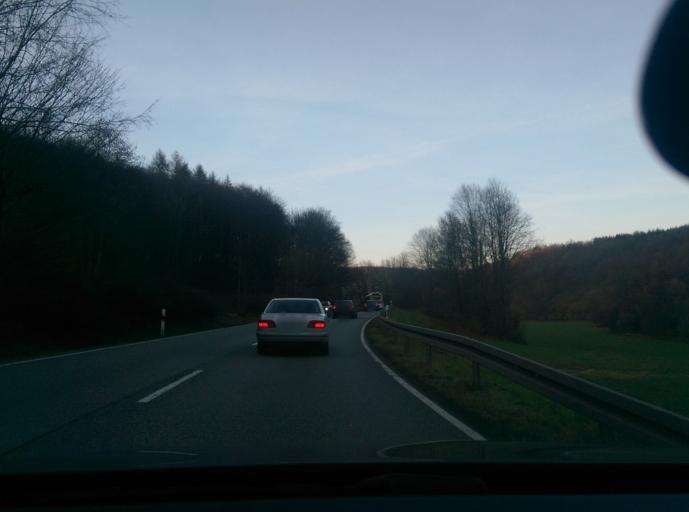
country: DE
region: Hesse
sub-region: Regierungsbezirk Kassel
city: Sontra
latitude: 51.0946
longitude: 9.9740
